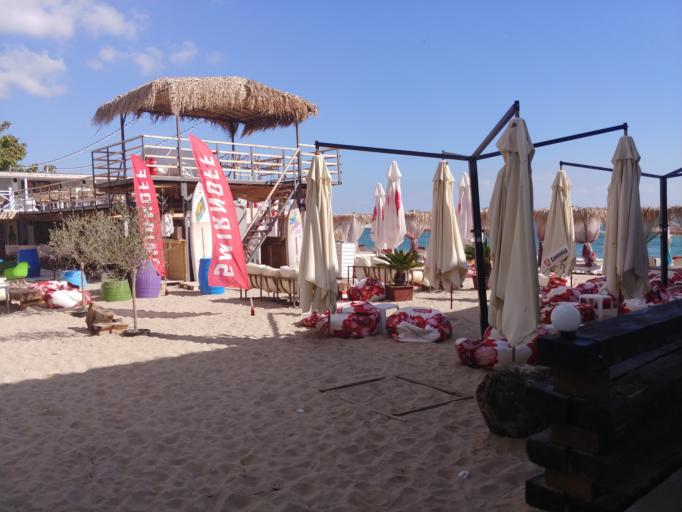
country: BG
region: Varna
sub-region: Obshtina Varna
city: Varna
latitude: 43.2026
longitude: 27.9243
